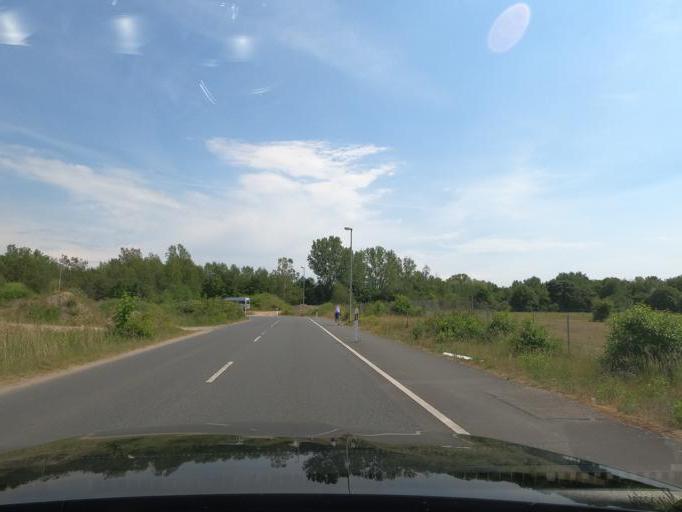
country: DE
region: Lower Saxony
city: Isernhagen Farster Bauerschaft
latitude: 52.4160
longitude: 9.8334
